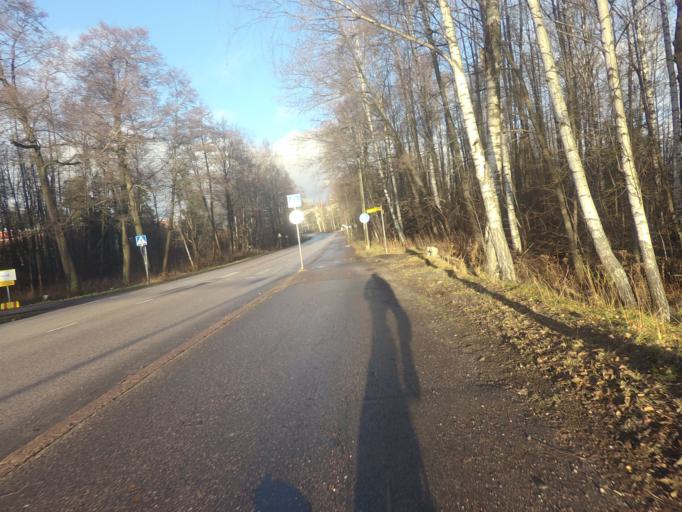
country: FI
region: Uusimaa
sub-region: Helsinki
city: Otaniemi
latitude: 60.1803
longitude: 24.8346
